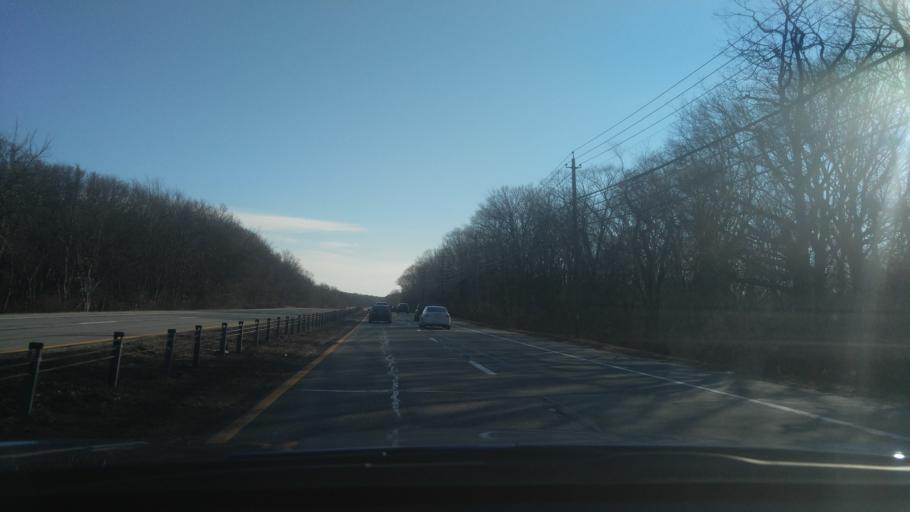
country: US
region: Rhode Island
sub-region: Washington County
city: Narragansett Pier
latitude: 41.4880
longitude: -71.4577
